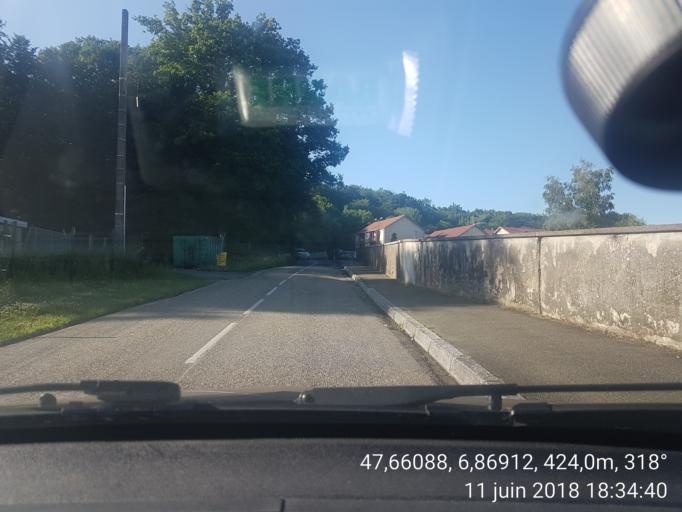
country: FR
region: Franche-Comte
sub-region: Territoire de Belfort
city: Offemont
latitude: 47.6608
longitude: 6.8692
